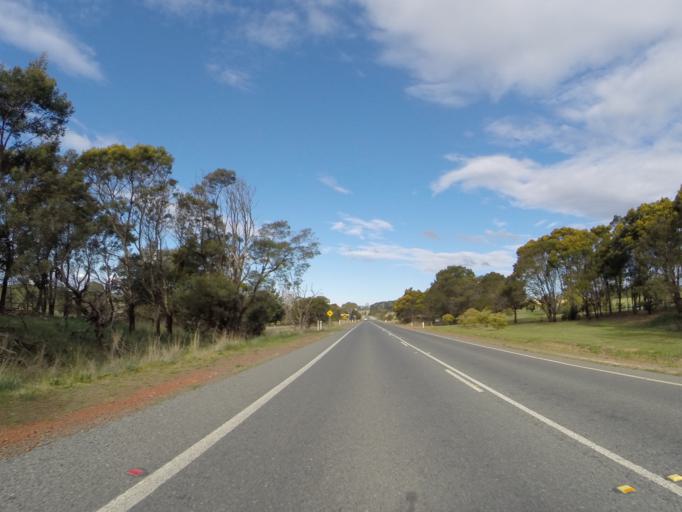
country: AU
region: New South Wales
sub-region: Wingecarribee
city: Bundanoon
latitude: -34.5852
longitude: 150.2805
